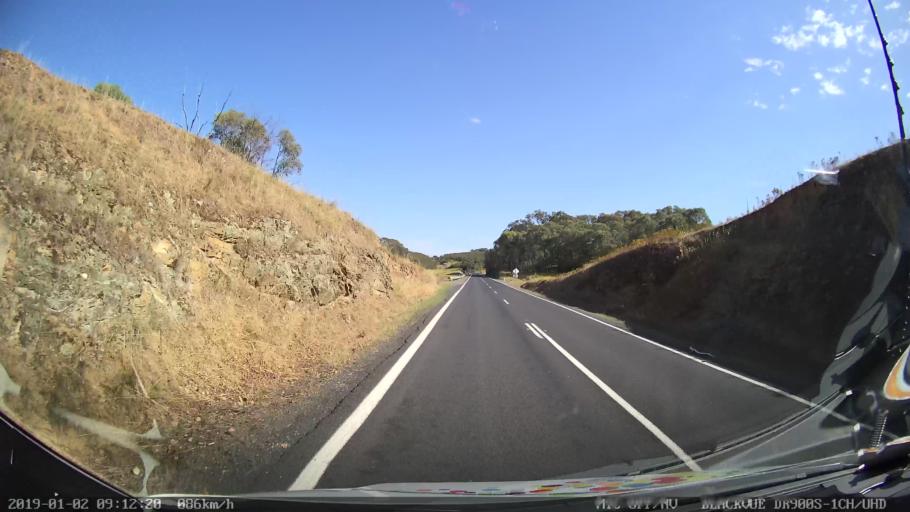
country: AU
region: New South Wales
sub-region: Tumut Shire
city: Tumut
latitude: -35.5017
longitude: 148.2724
